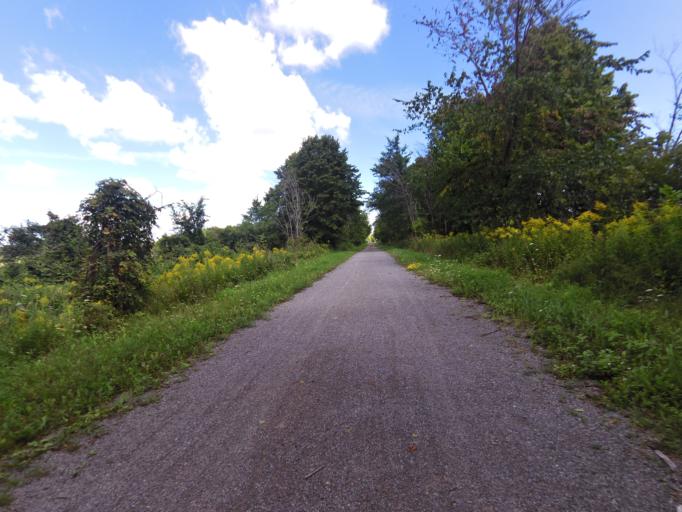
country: CA
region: Ontario
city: Ottawa
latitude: 45.2957
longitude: -75.6276
